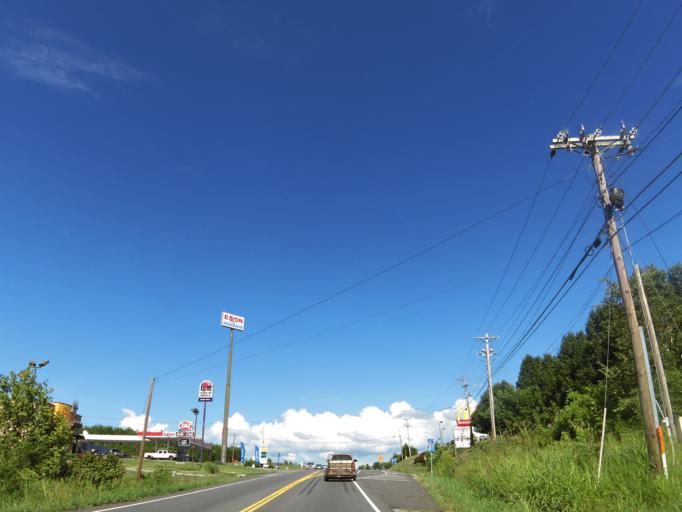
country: US
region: Tennessee
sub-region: Greene County
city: Mosheim
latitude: 36.2249
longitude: -83.0468
